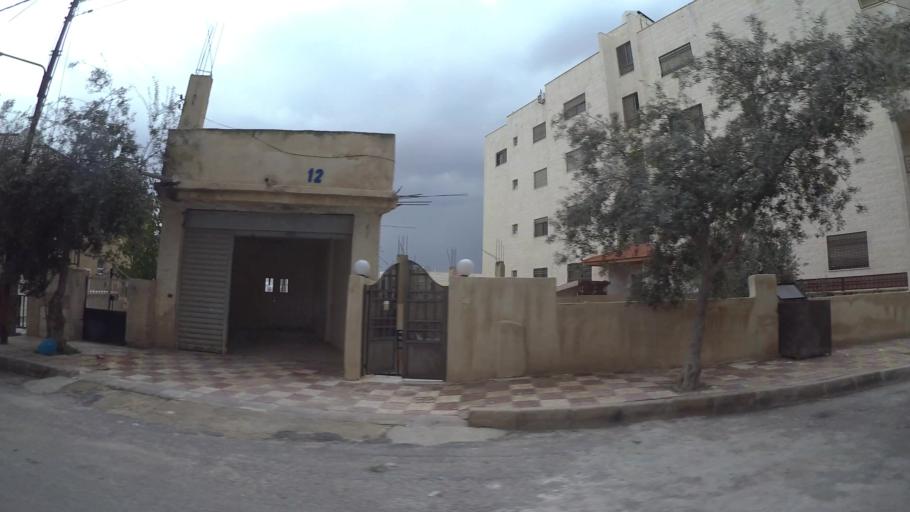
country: JO
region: Amman
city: Amman
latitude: 32.0094
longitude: 35.9496
